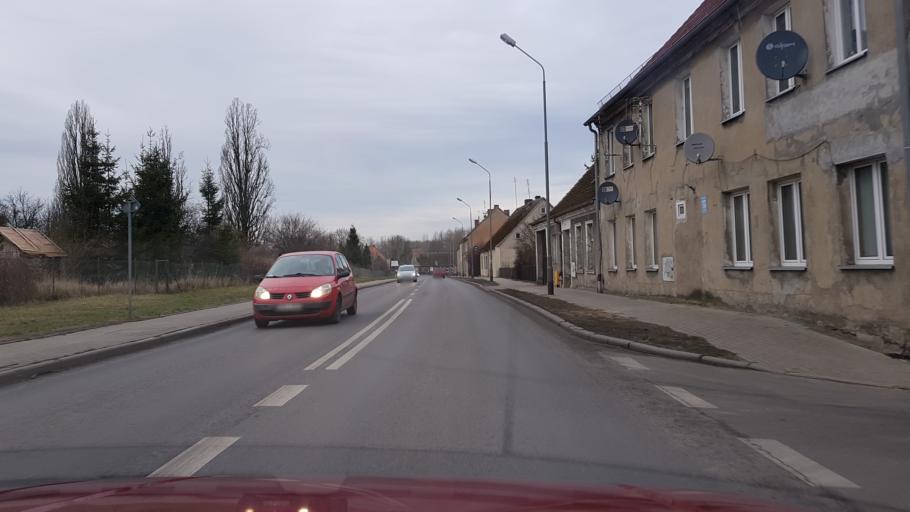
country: PL
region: West Pomeranian Voivodeship
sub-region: Powiat policki
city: Police
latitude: 53.5535
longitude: 14.5714
